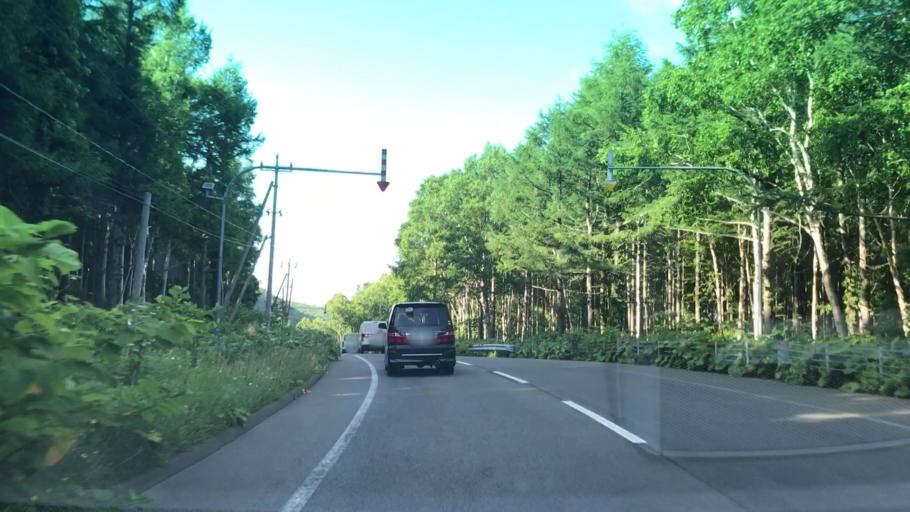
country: JP
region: Hokkaido
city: Otaru
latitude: 43.1132
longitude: 141.0093
